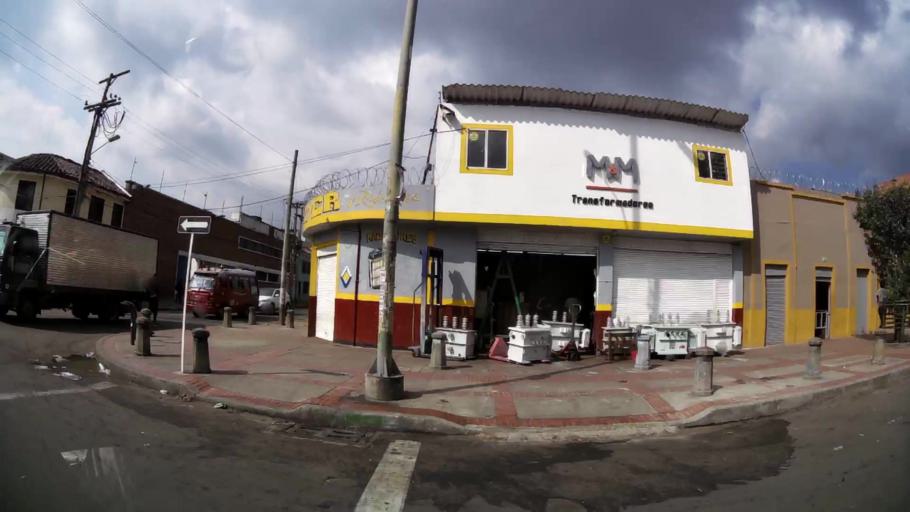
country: CO
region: Bogota D.C.
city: Bogota
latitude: 4.6142
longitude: -74.0796
